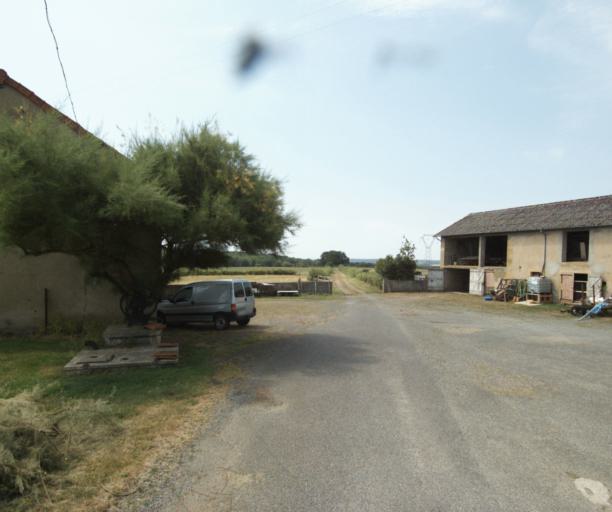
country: FR
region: Bourgogne
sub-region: Departement de Saone-et-Loire
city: Gueugnon
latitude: 46.5833
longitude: 4.0755
